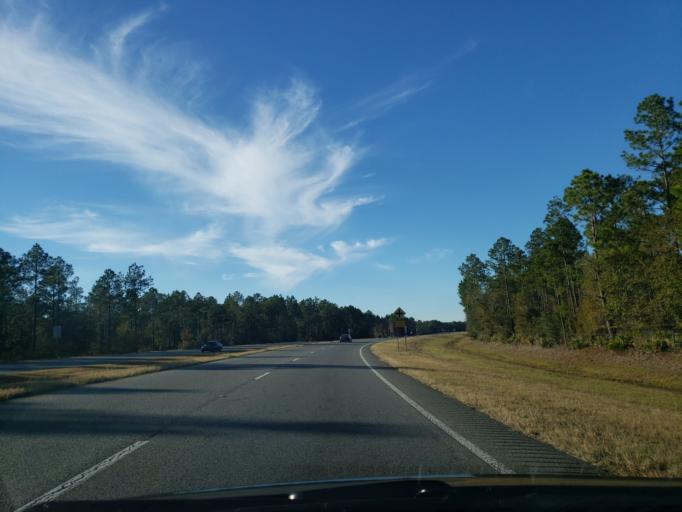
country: US
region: Georgia
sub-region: Ware County
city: Deenwood
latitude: 31.2099
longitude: -82.4145
